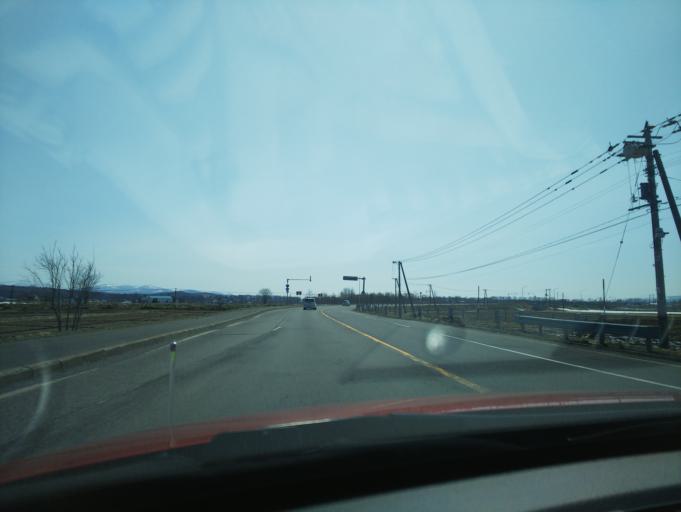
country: JP
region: Hokkaido
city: Nayoro
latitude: 44.3160
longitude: 142.4573
